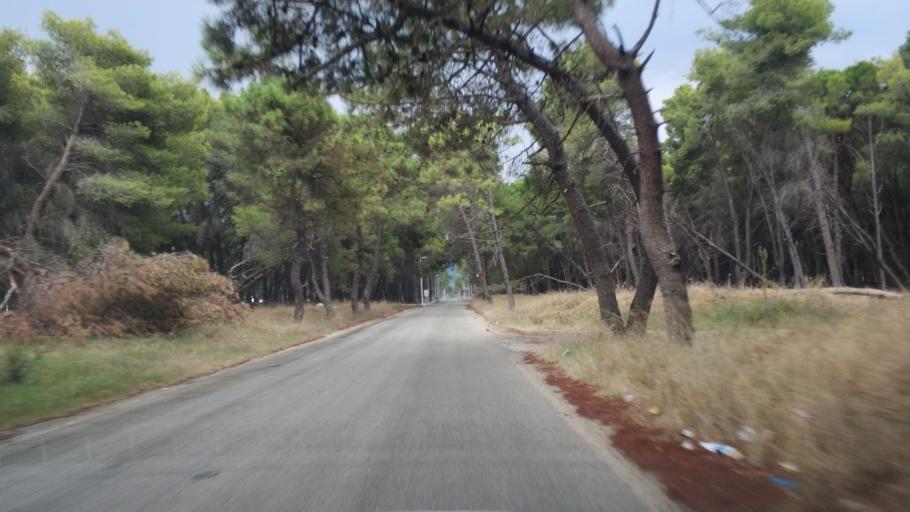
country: AL
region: Vlore
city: Vlore
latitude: 40.4682
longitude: 19.4606
